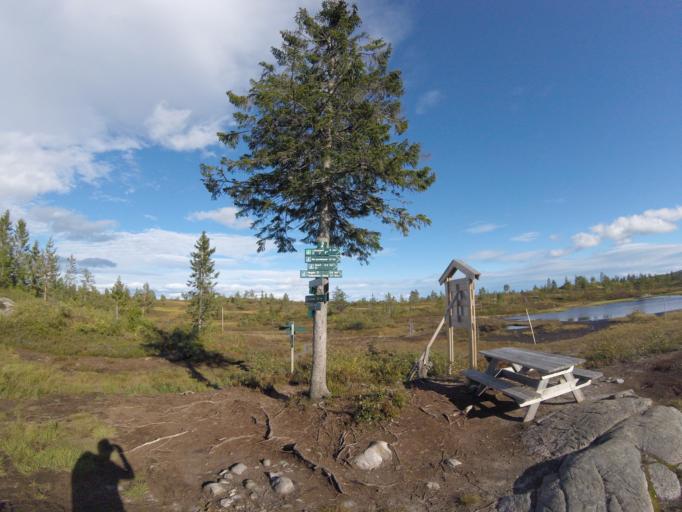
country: NO
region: Buskerud
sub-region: Flesberg
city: Lampeland
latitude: 59.7744
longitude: 9.4043
